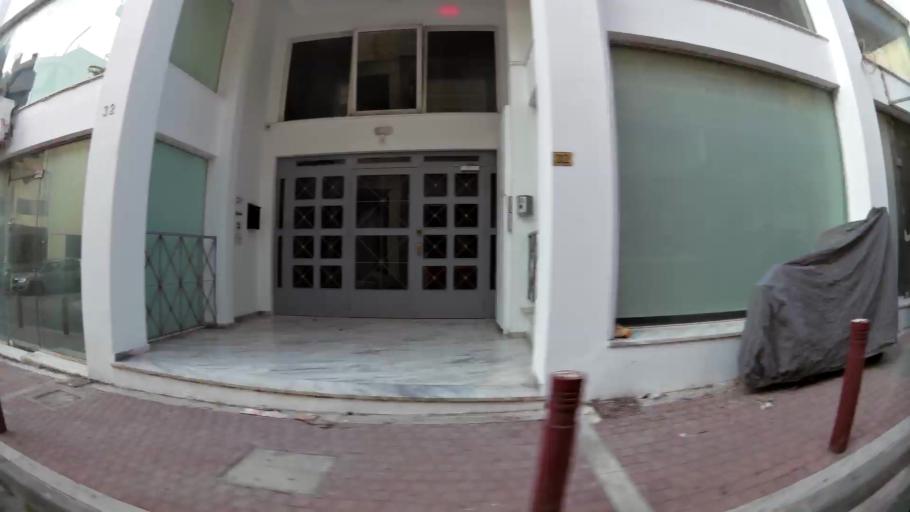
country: GR
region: Attica
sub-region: Nomarchia Athinas
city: Dhafni
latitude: 37.9531
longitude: 23.7346
